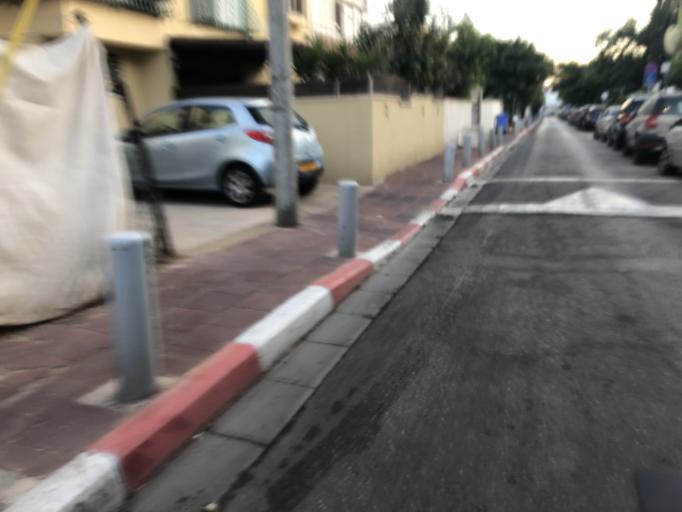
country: IL
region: Tel Aviv
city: Giv`atayim
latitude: 32.0699
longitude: 34.8182
